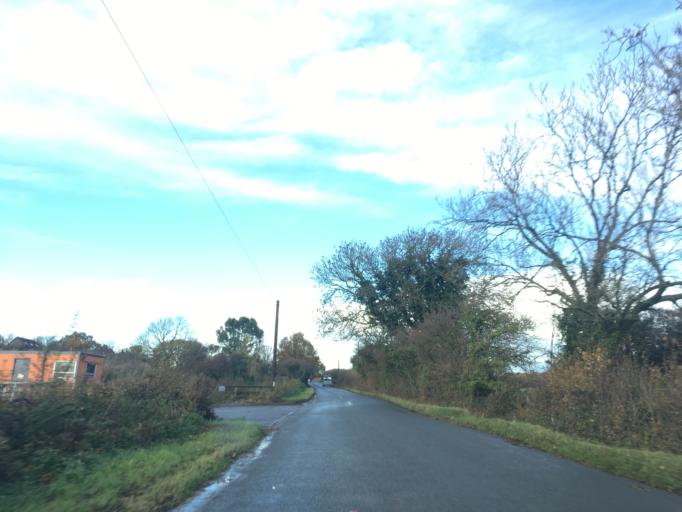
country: GB
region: England
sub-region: South Gloucestershire
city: Siston
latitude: 51.5062
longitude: -2.4615
